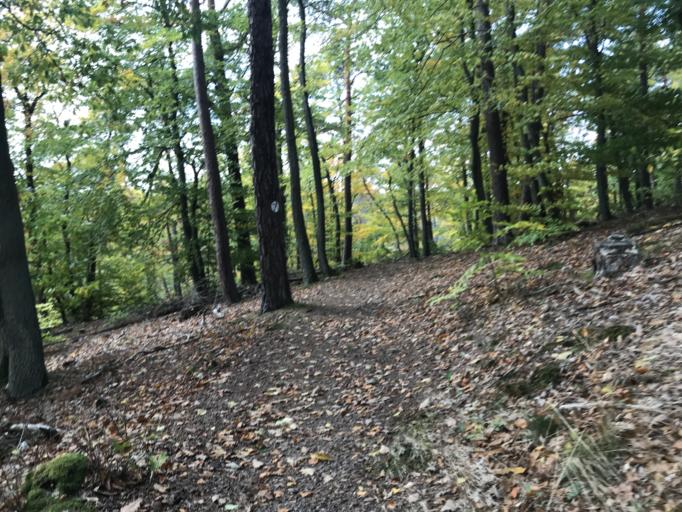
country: DE
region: Rheinland-Pfalz
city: Dannenfels
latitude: 49.6518
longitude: 7.9713
